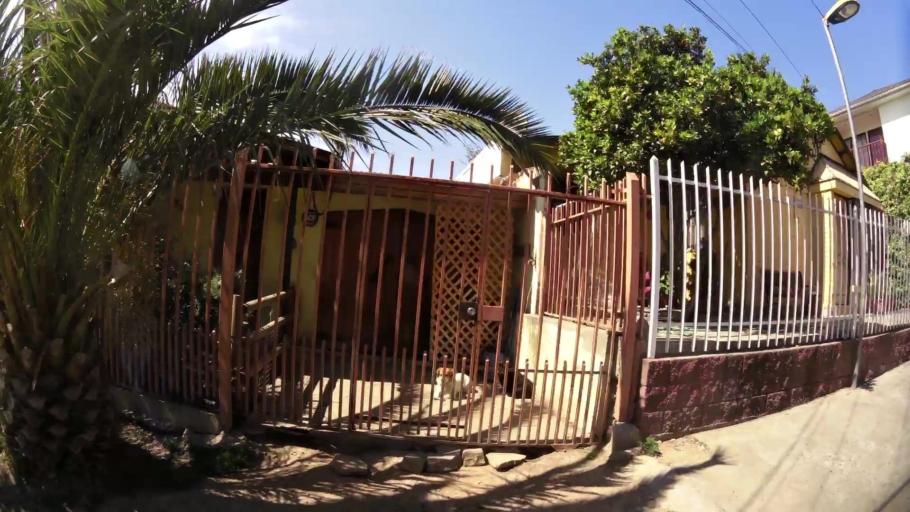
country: CL
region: Santiago Metropolitan
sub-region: Provincia de Santiago
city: Lo Prado
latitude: -33.4917
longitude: -70.7408
